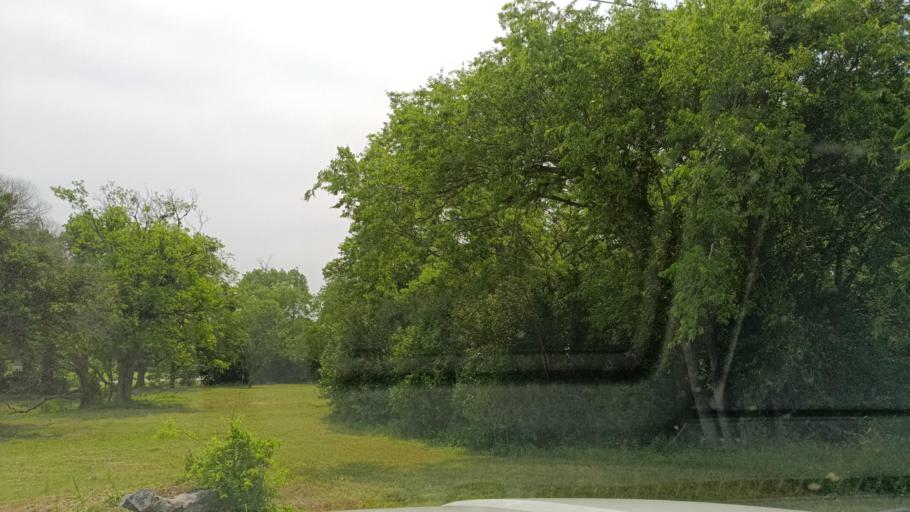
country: US
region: Texas
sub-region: Bell County
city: Temple
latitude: 31.0602
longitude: -97.3376
